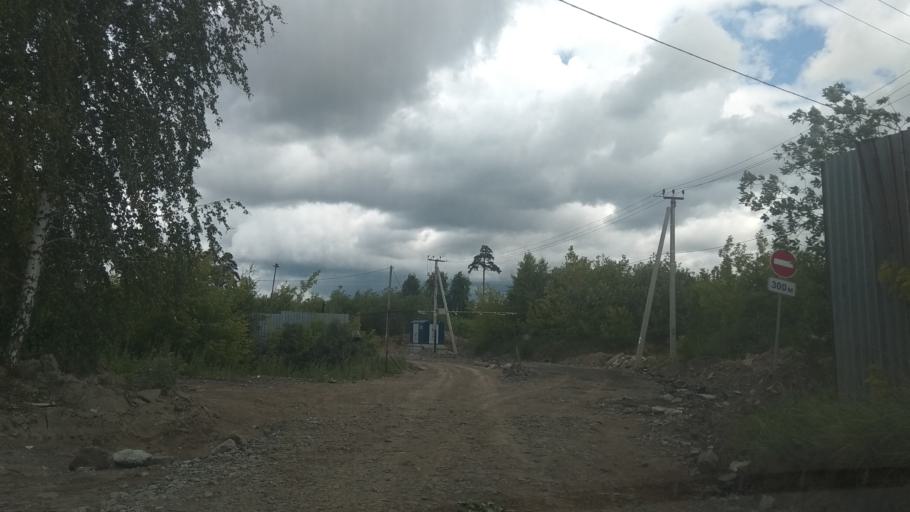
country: RU
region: Sverdlovsk
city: Verkhnyaya Pyshma
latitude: 56.9193
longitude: 60.5712
